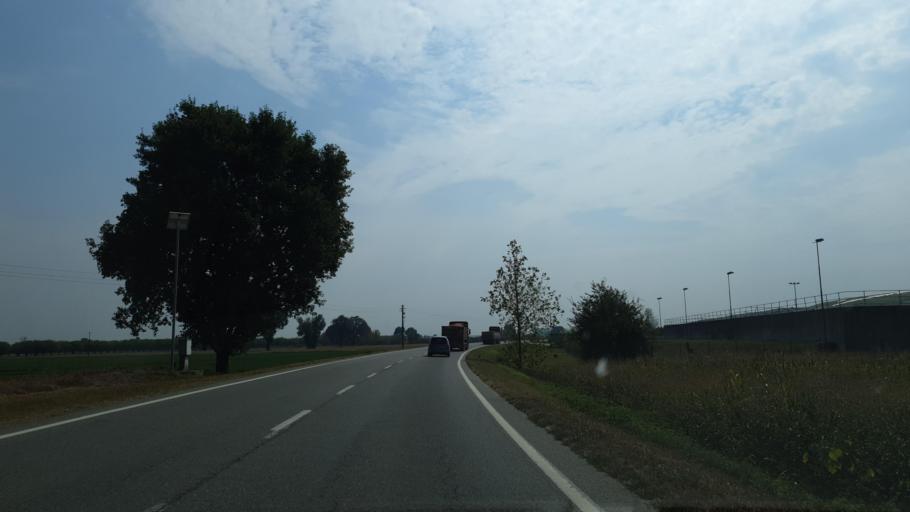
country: IT
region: Lombardy
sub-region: Provincia di Cremona
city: San Daniele Po
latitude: 45.0684
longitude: 10.1912
